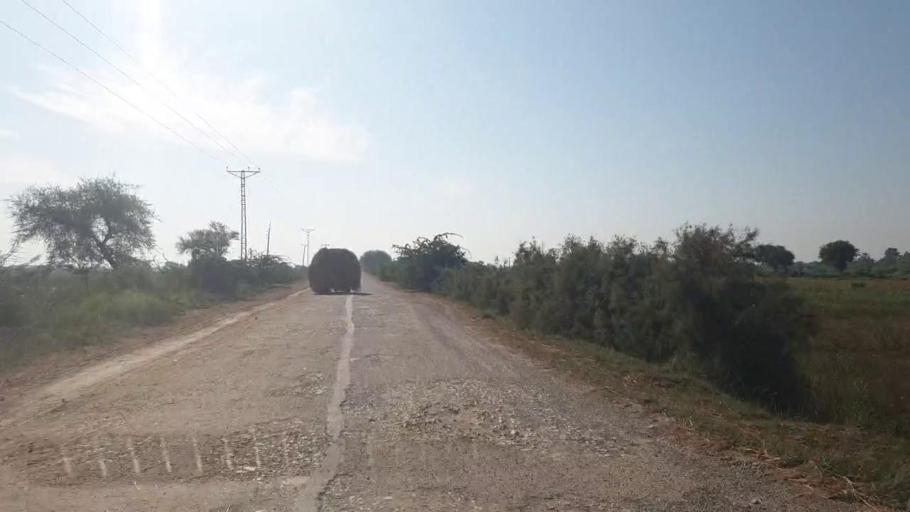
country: PK
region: Sindh
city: Talhar
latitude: 24.9156
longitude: 68.8165
